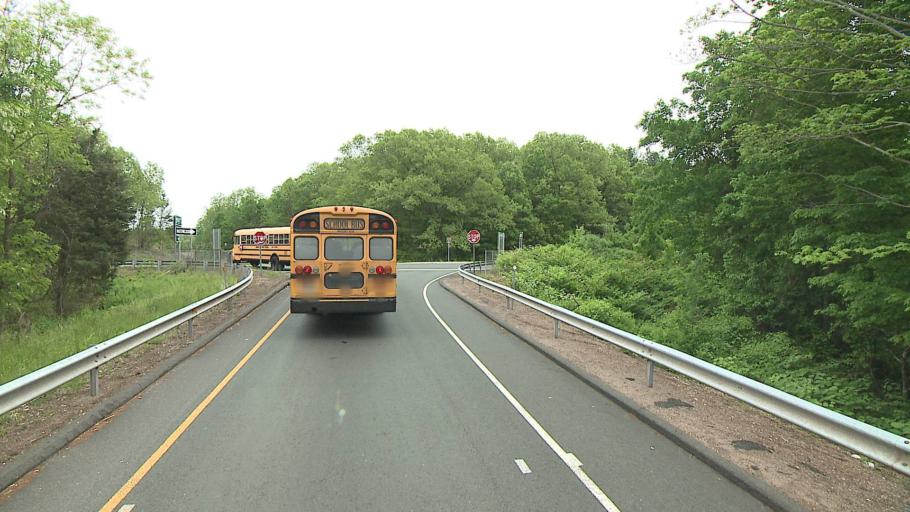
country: US
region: Connecticut
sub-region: Hartford County
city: Manchester
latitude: 41.7644
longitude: -72.4899
